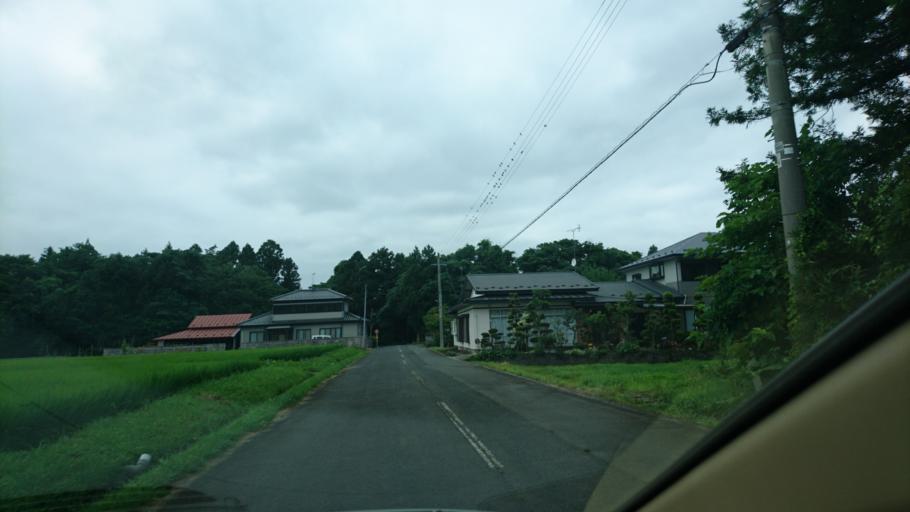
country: JP
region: Iwate
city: Kitakami
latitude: 39.2287
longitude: 141.1003
